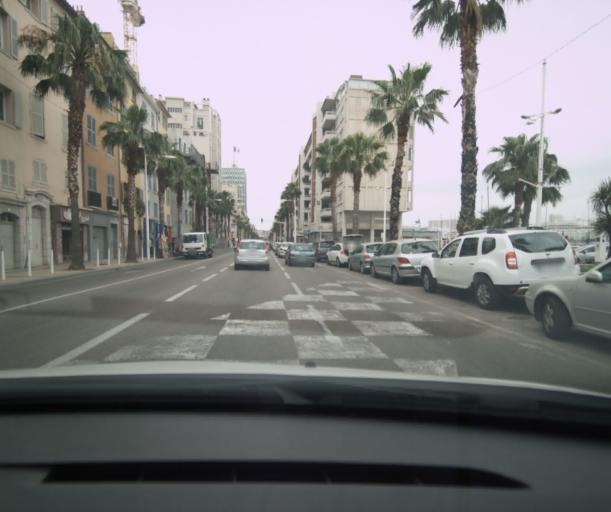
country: FR
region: Provence-Alpes-Cote d'Azur
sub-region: Departement du Var
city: Toulon
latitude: 43.1217
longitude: 5.9293
